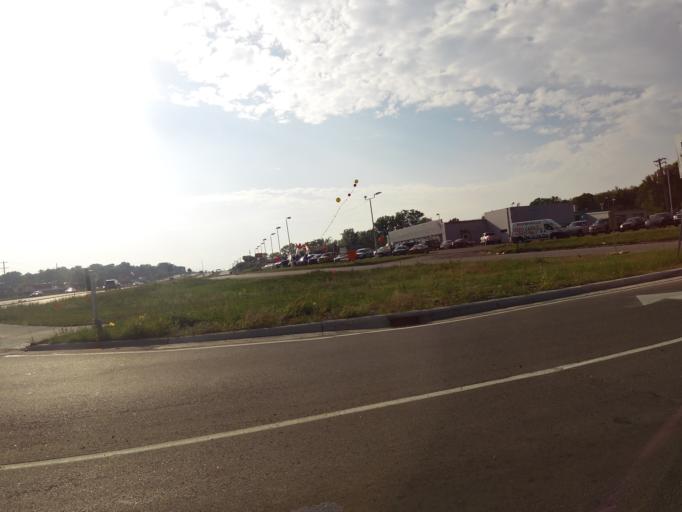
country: US
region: Minnesota
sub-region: Washington County
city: Oak Park Heights
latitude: 45.0361
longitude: -92.8076
